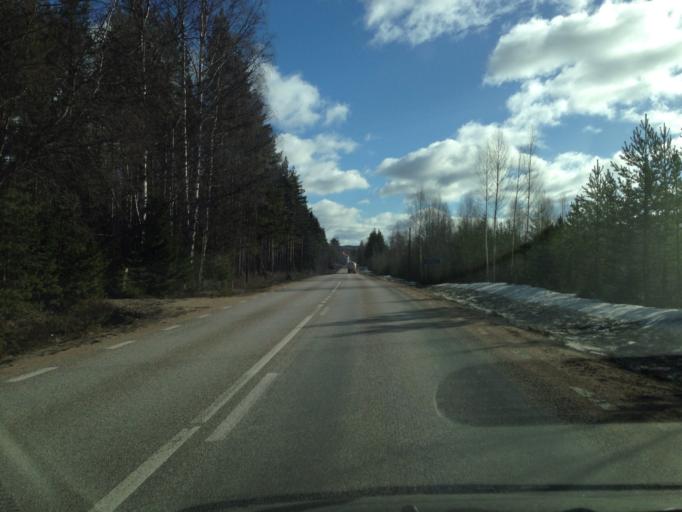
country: SE
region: Gaevleborg
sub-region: Ljusdals Kommun
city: Farila
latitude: 61.9875
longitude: 15.2849
